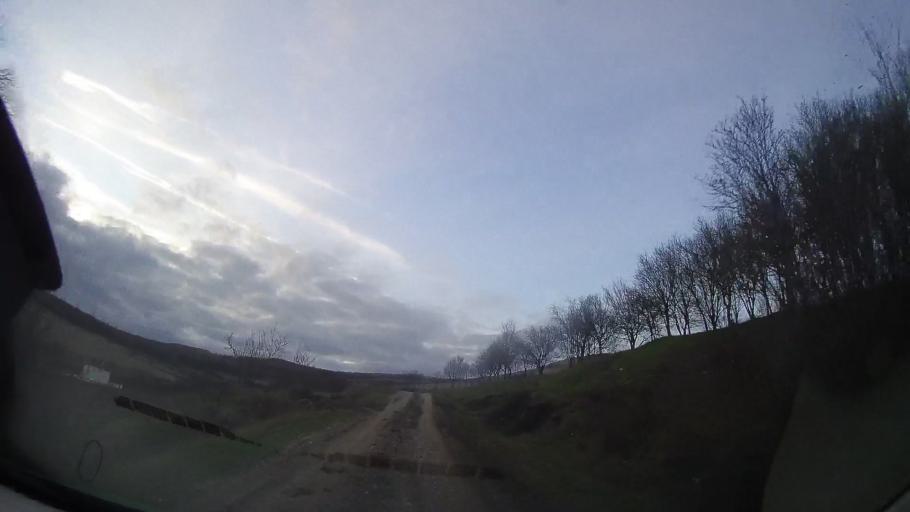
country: RO
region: Cluj
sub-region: Comuna Palatca
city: Palatca
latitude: 46.8569
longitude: 24.0374
